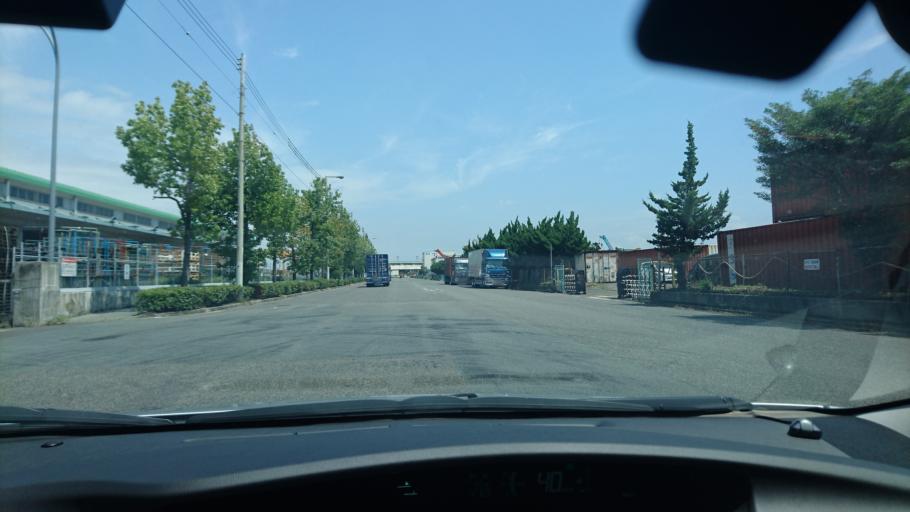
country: JP
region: Hyogo
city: Kobe
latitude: 34.6737
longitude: 135.2245
